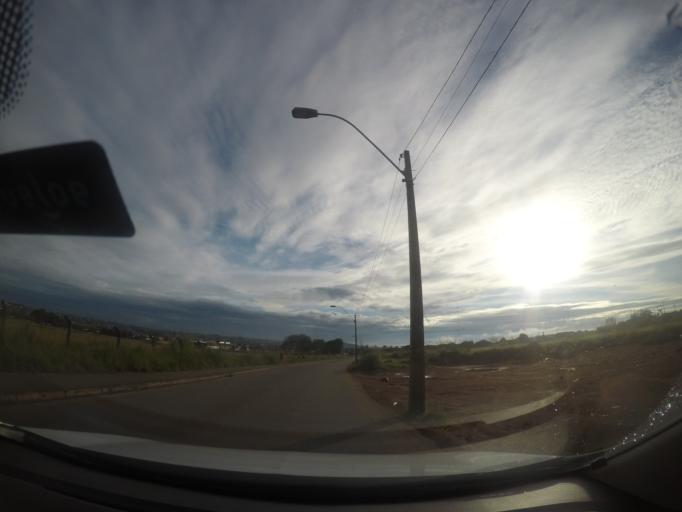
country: BR
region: Goias
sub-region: Goiania
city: Goiania
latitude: -16.6416
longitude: -49.3193
